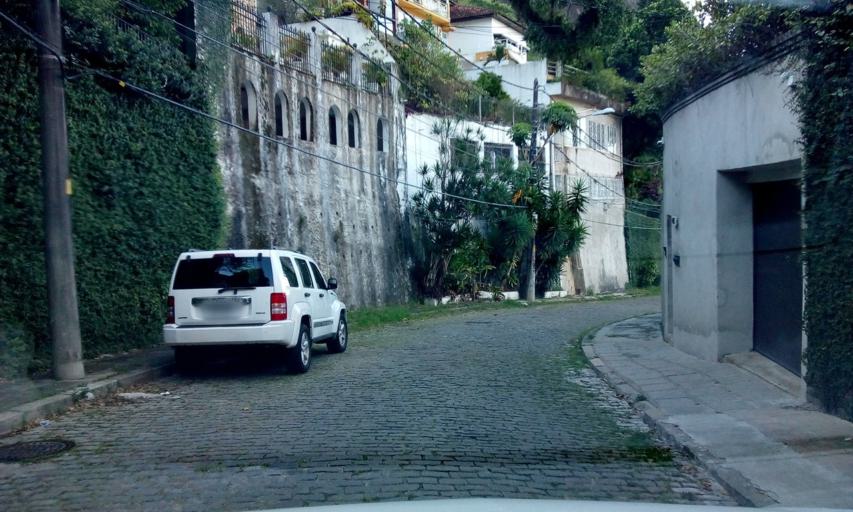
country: BR
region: Rio de Janeiro
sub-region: Rio De Janeiro
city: Rio de Janeiro
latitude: -22.9652
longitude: -43.1986
